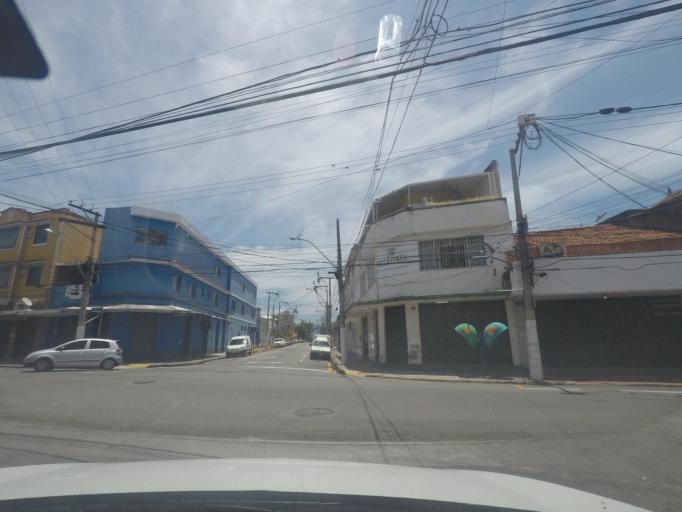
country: BR
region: Rio de Janeiro
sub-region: Niteroi
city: Niteroi
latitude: -22.8829
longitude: -43.1216
